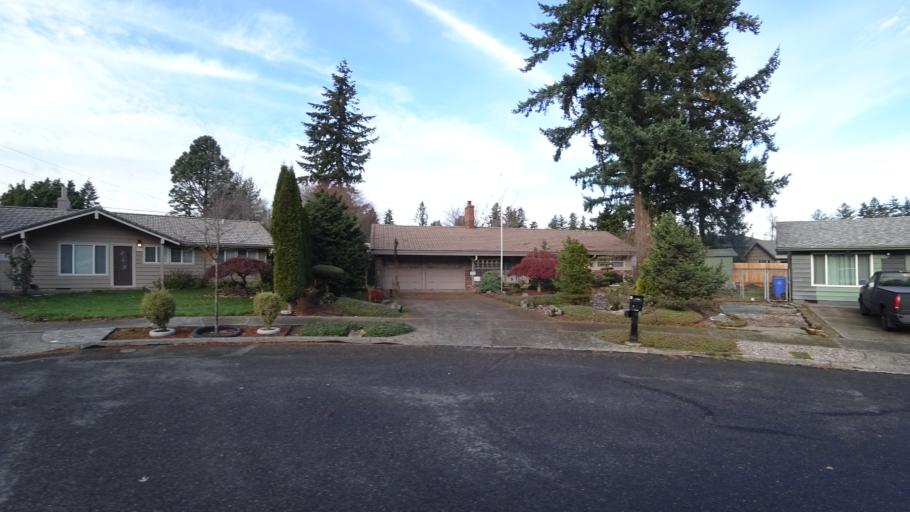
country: US
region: Oregon
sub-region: Multnomah County
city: Lents
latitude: 45.5320
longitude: -122.5280
